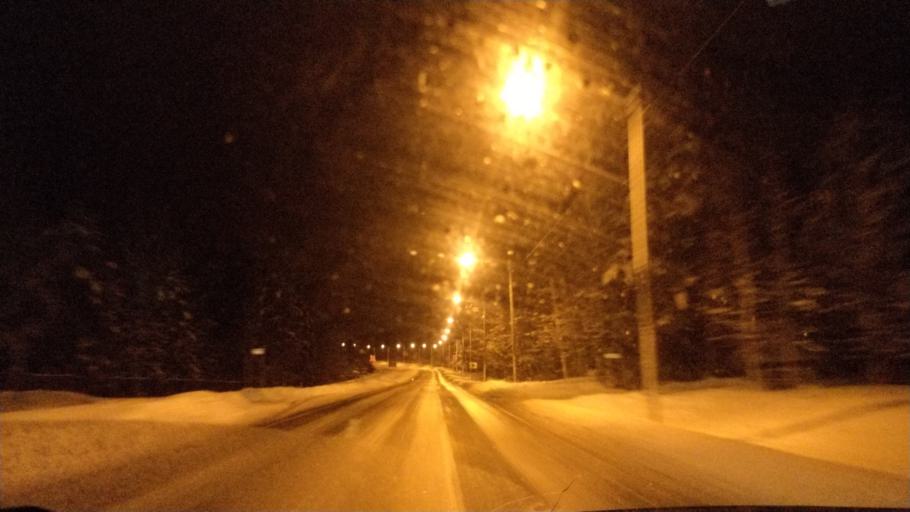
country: FI
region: Lapland
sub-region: Rovaniemi
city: Rovaniemi
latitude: 66.2704
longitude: 25.3309
